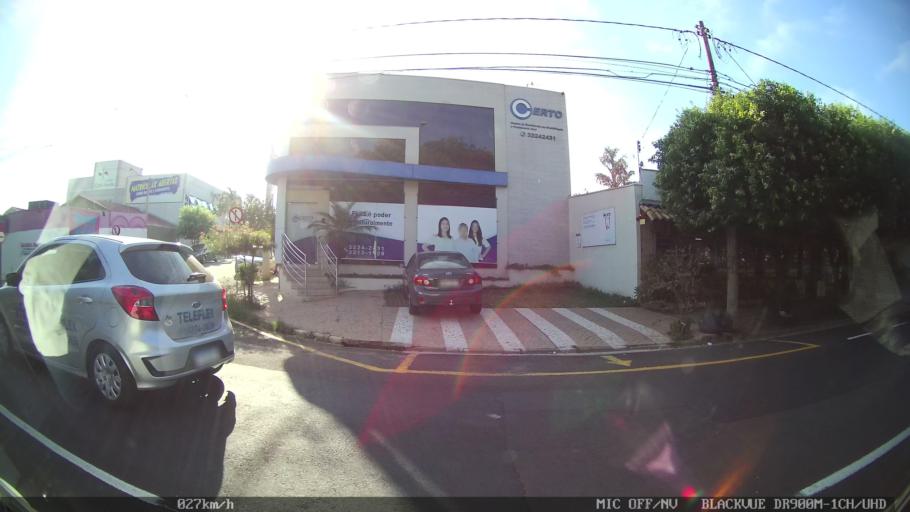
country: BR
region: Sao Paulo
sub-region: Sao Jose Do Rio Preto
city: Sao Jose do Rio Preto
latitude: -20.8180
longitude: -49.3655
